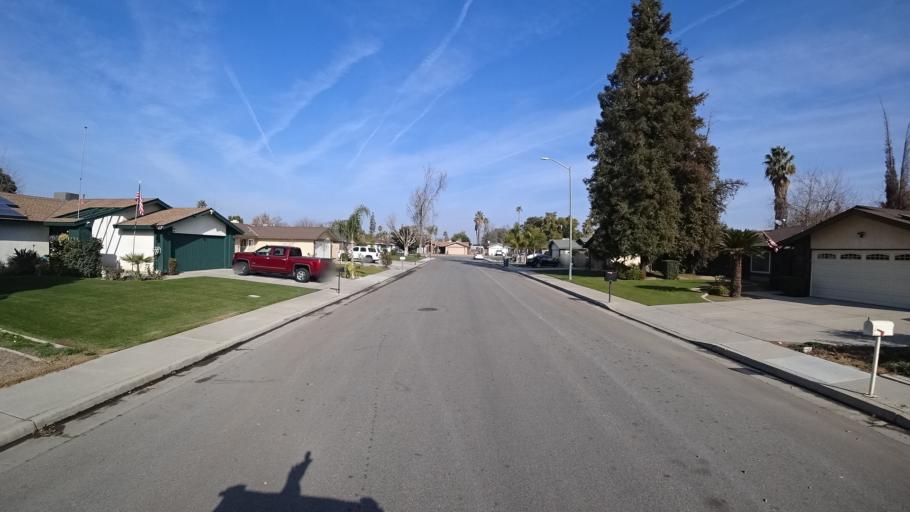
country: US
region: California
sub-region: Kern County
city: Bakersfield
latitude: 35.3201
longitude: -119.0422
